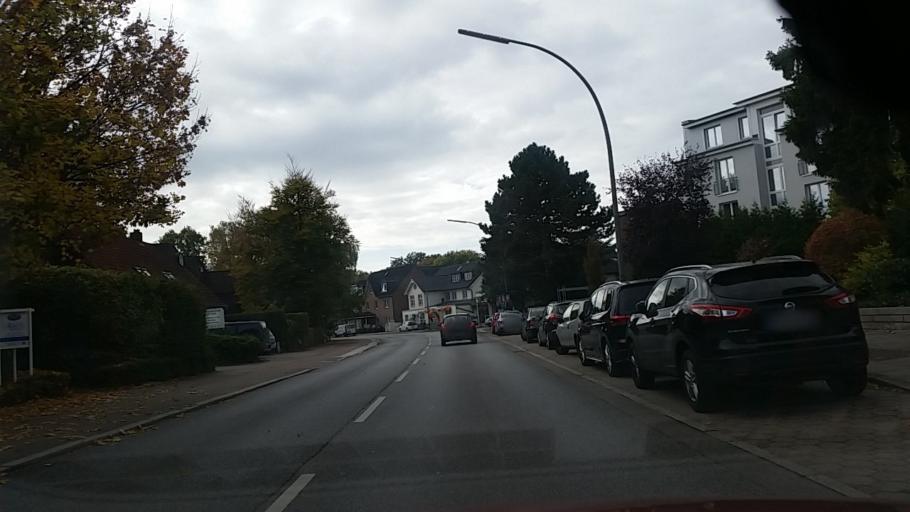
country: DE
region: Hamburg
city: Hummelsbuettel
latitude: 53.6407
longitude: 10.0368
